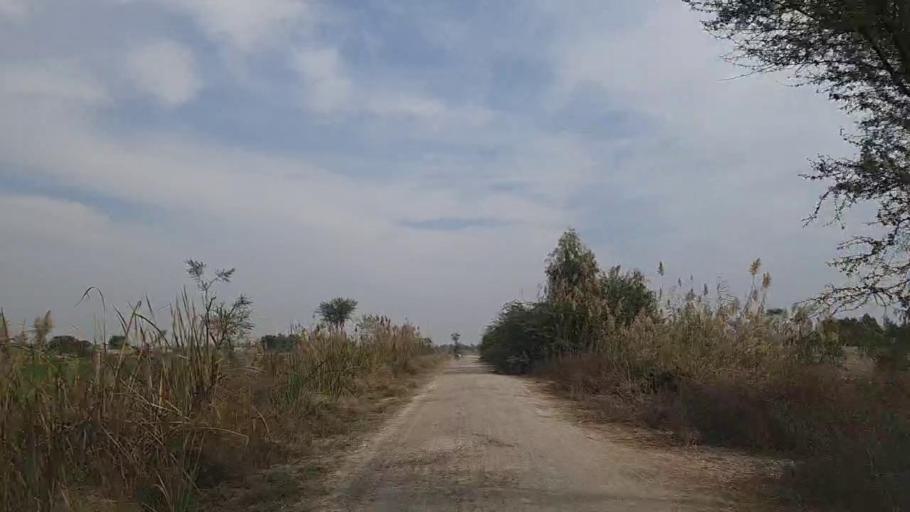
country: PK
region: Sindh
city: Daur
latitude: 26.4992
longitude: 68.3935
